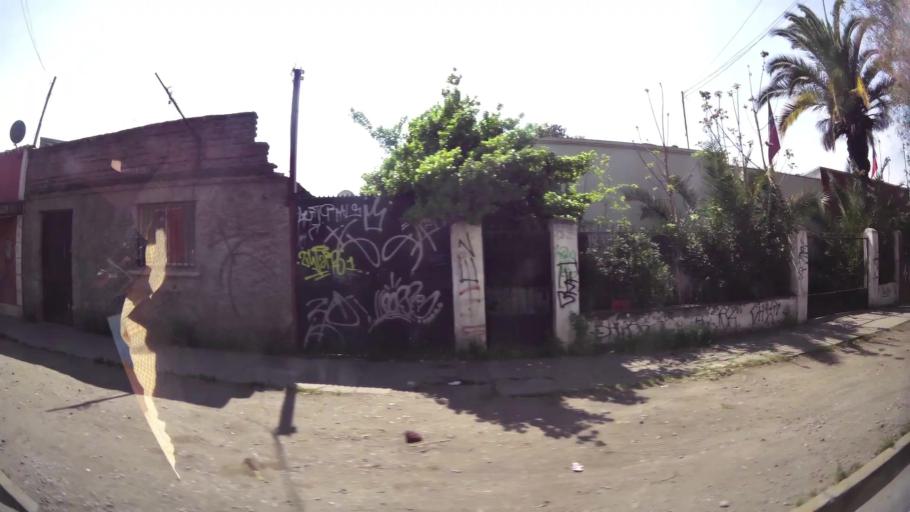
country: CL
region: Santiago Metropolitan
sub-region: Provincia de Santiago
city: Lo Prado
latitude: -33.4312
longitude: -70.7180
